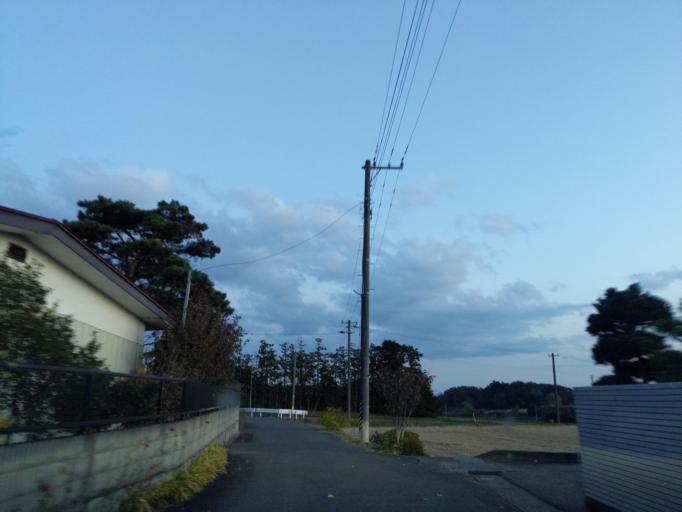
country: JP
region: Fukushima
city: Koriyama
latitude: 37.4614
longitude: 140.3200
